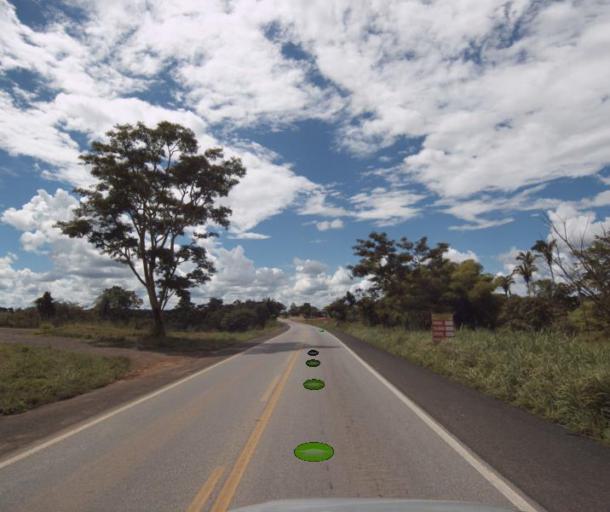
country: BR
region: Goias
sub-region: Porangatu
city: Porangatu
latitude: -13.8920
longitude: -49.0573
